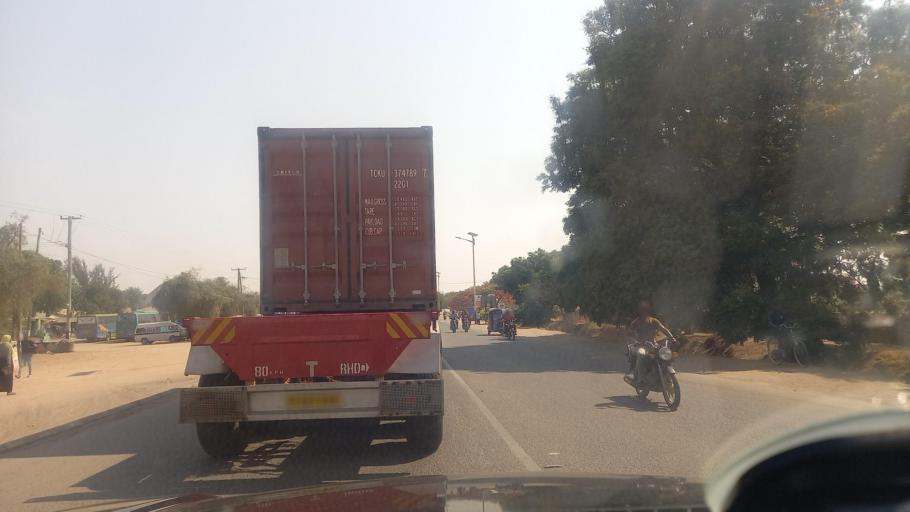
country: TZ
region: Dodoma
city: Dodoma
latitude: -6.1780
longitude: 35.7580
